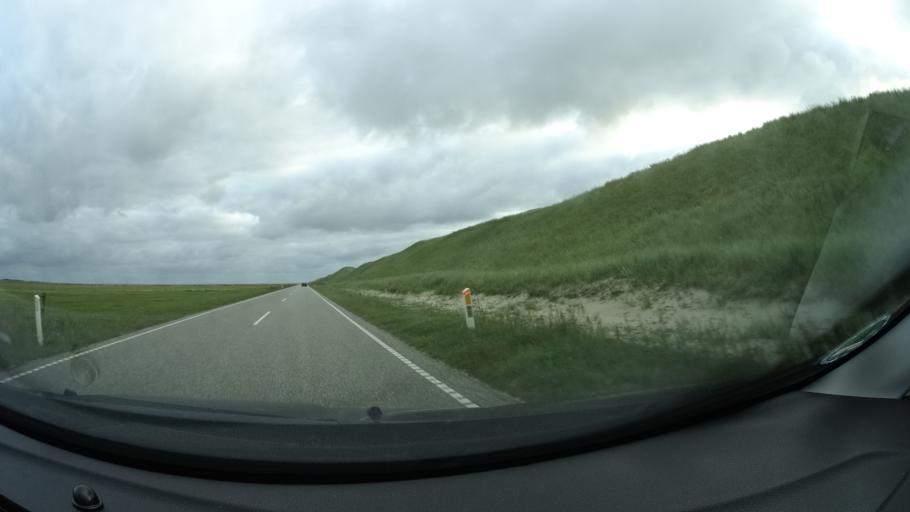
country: DK
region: Central Jutland
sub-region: Lemvig Kommune
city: Harboore
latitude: 56.4282
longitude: 8.1238
